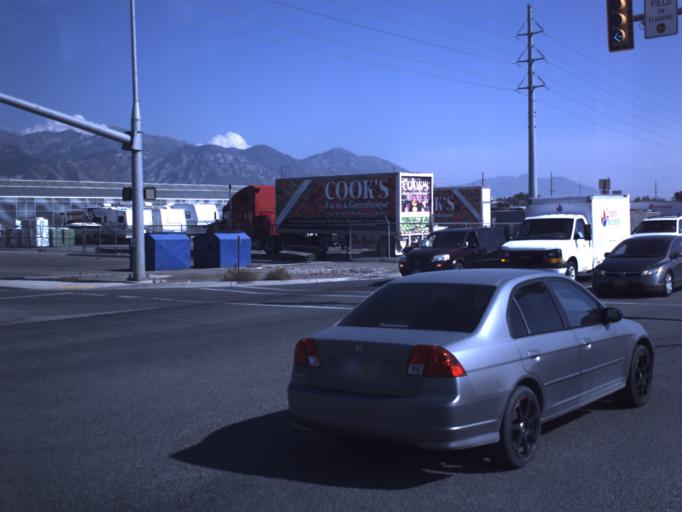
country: US
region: Utah
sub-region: Utah County
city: Lindon
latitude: 40.3263
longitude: -111.7374
